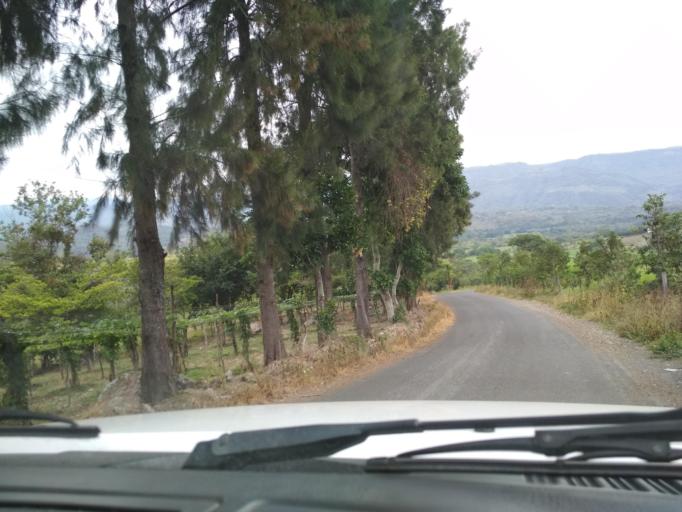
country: MX
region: Veracruz
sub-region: Actopan
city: Trapiche del Rosario
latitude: 19.5629
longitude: -96.7923
